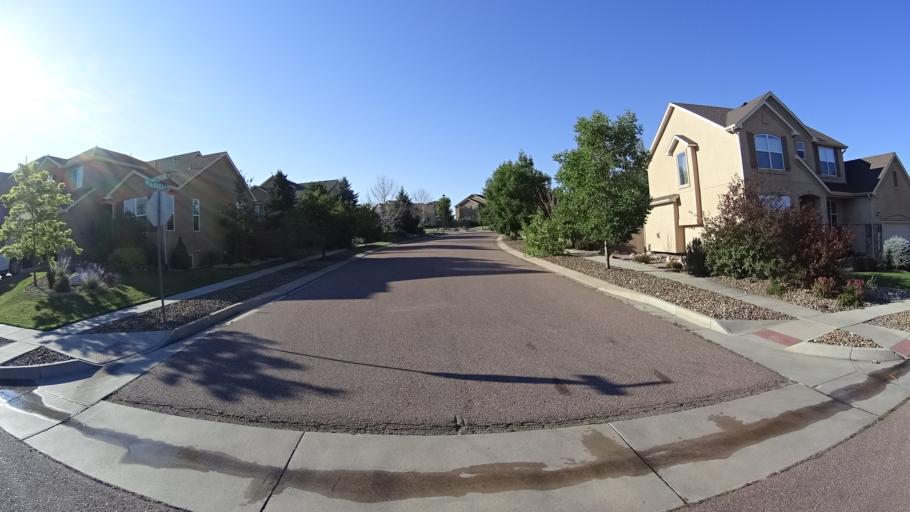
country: US
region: Colorado
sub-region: El Paso County
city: Black Forest
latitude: 38.9866
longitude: -104.7731
